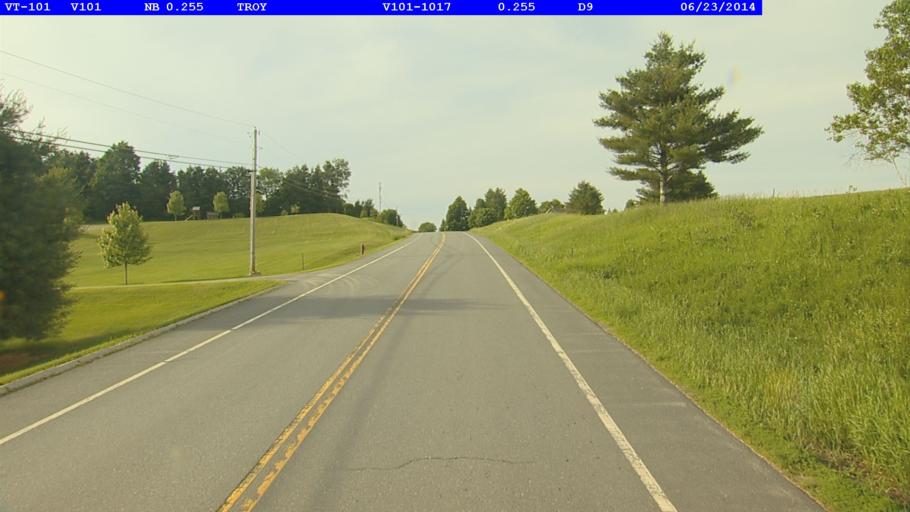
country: US
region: Vermont
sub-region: Orleans County
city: Newport
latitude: 44.9073
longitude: -72.4051
